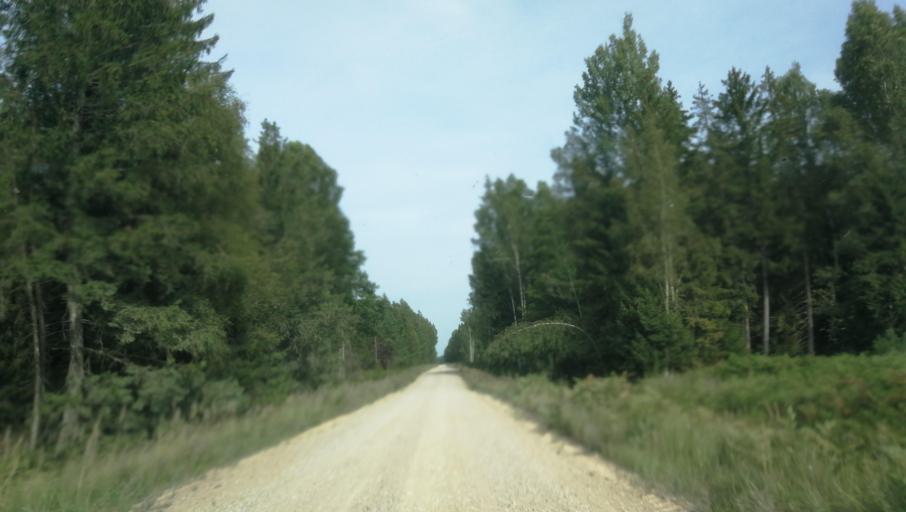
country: LV
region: Durbe
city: Liegi
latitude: 56.7789
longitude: 21.3518
